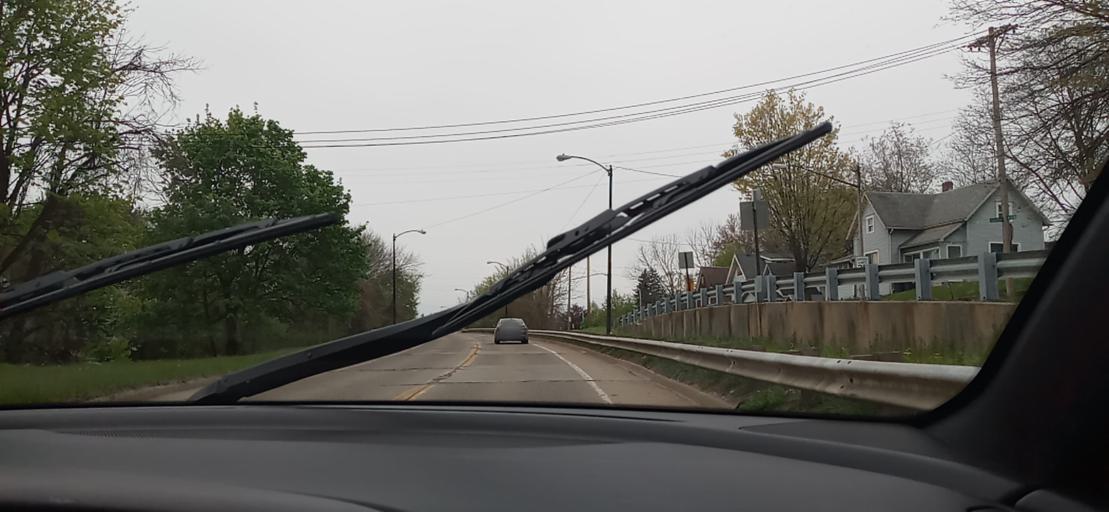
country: US
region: Ohio
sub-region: Summit County
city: Portage Lakes
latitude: 41.0470
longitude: -81.5479
